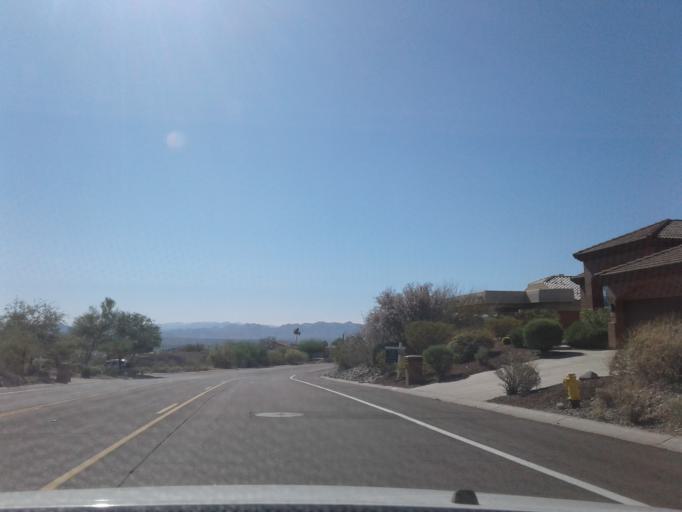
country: US
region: Arizona
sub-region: Maricopa County
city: Fountain Hills
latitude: 33.5909
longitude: -111.7428
